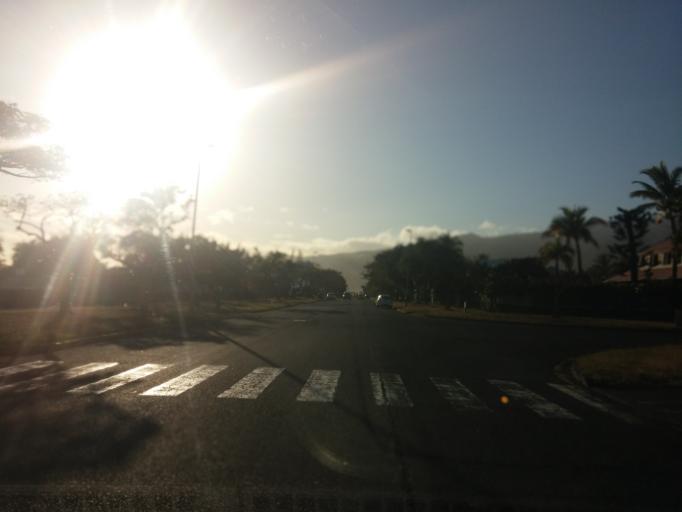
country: RE
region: Reunion
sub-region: Reunion
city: Le Port
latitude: -20.9340
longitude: 55.3059
